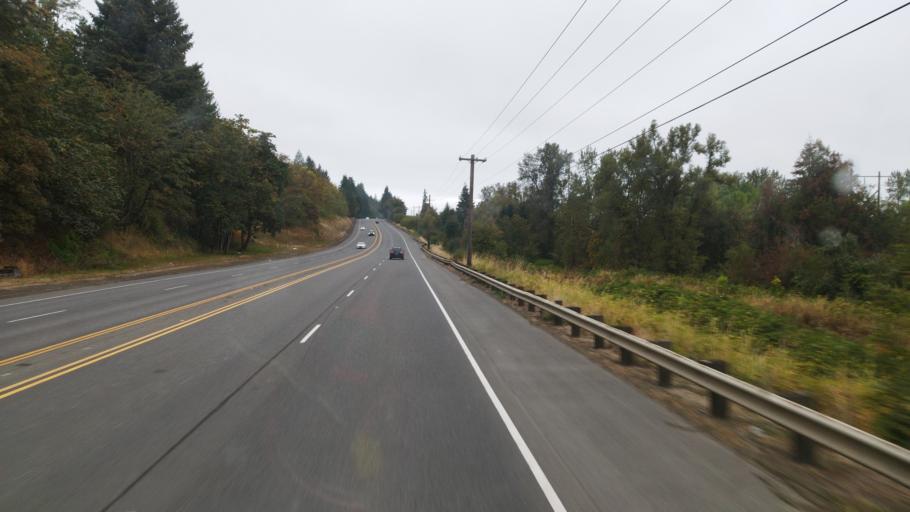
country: US
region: Oregon
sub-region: Washington County
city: Bethany
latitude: 45.6345
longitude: -122.8274
